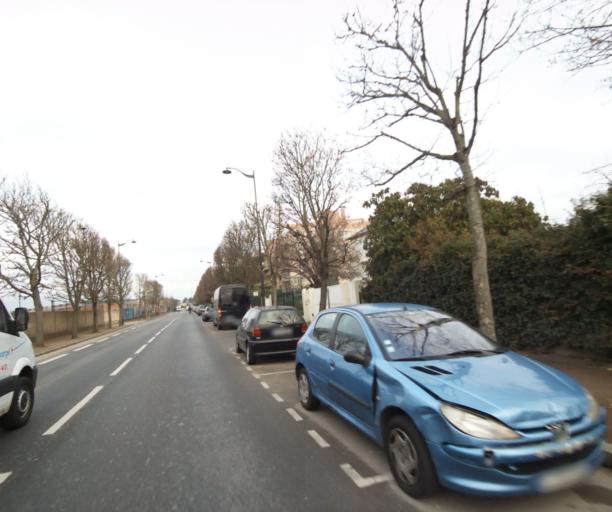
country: FR
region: Ile-de-France
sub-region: Departement des Hauts-de-Seine
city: Rueil-Malmaison
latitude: 48.8722
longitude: 2.2028
